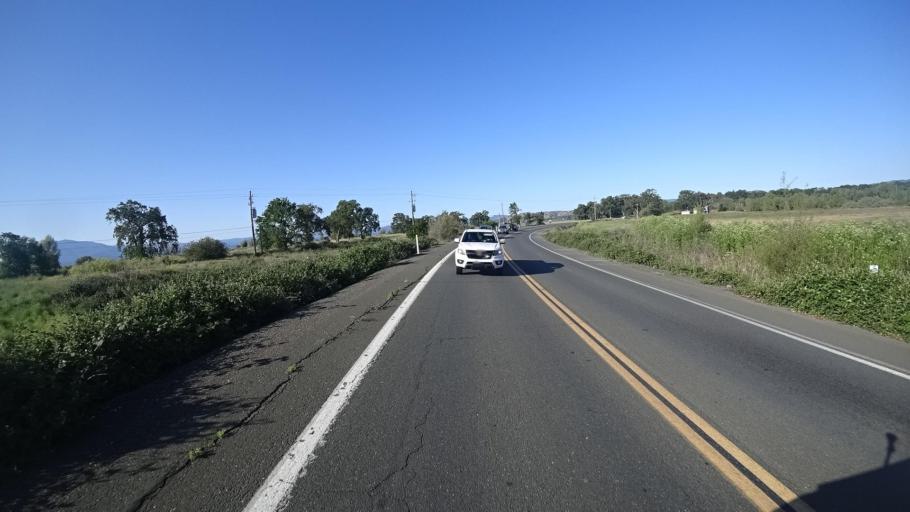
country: US
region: California
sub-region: Lake County
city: Nice
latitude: 39.1210
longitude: -122.8771
